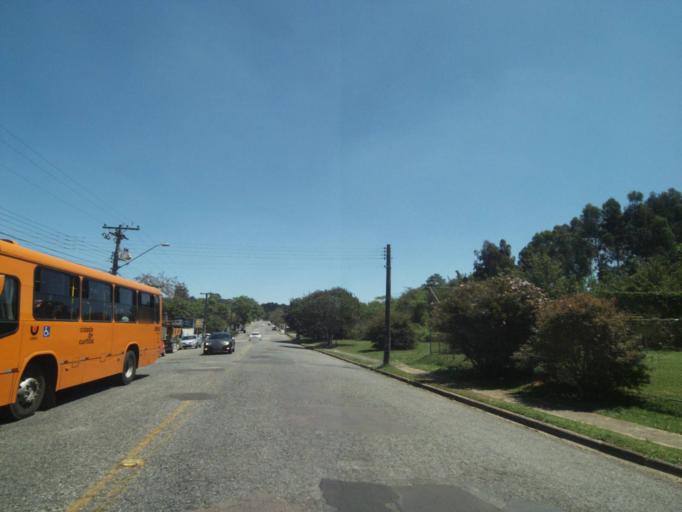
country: BR
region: Parana
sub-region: Pinhais
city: Pinhais
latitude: -25.3952
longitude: -49.2199
